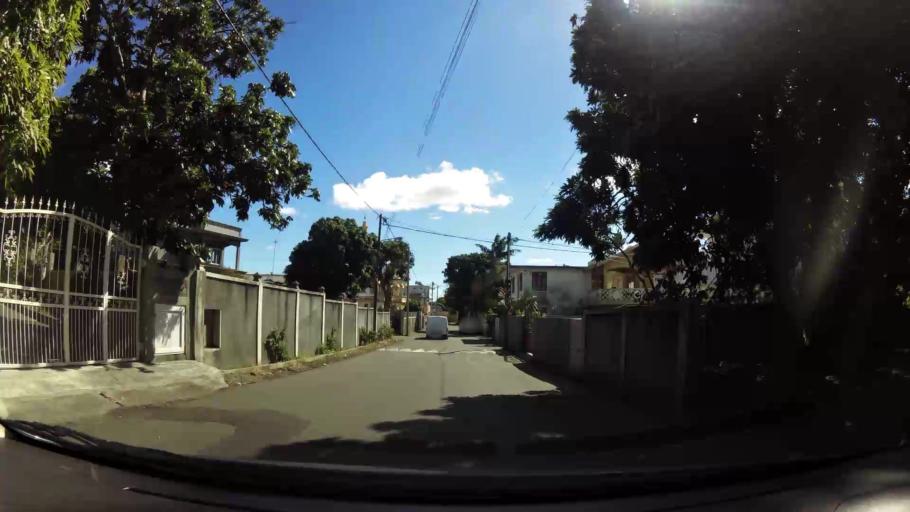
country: MU
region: Plaines Wilhems
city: Vacoas
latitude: -20.2918
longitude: 57.4788
